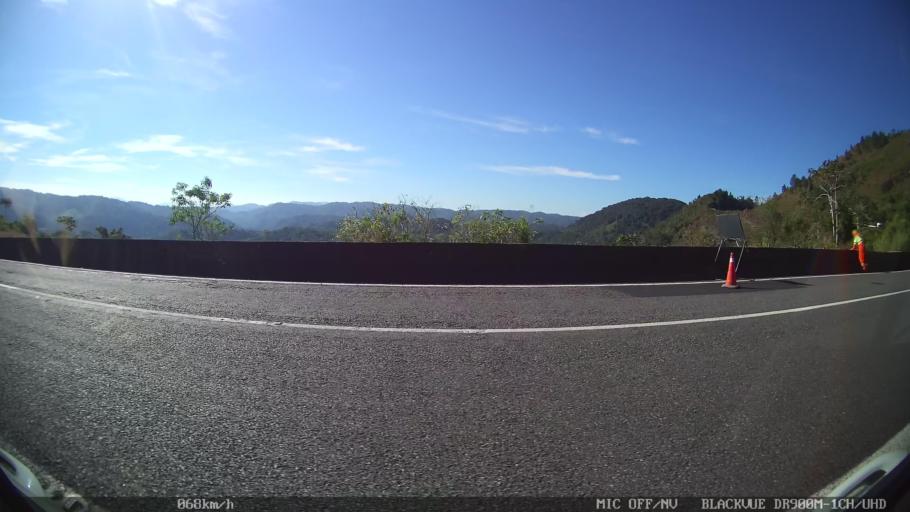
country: BR
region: Sao Paulo
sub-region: Cajati
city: Cajati
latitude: -24.9549
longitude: -48.4543
